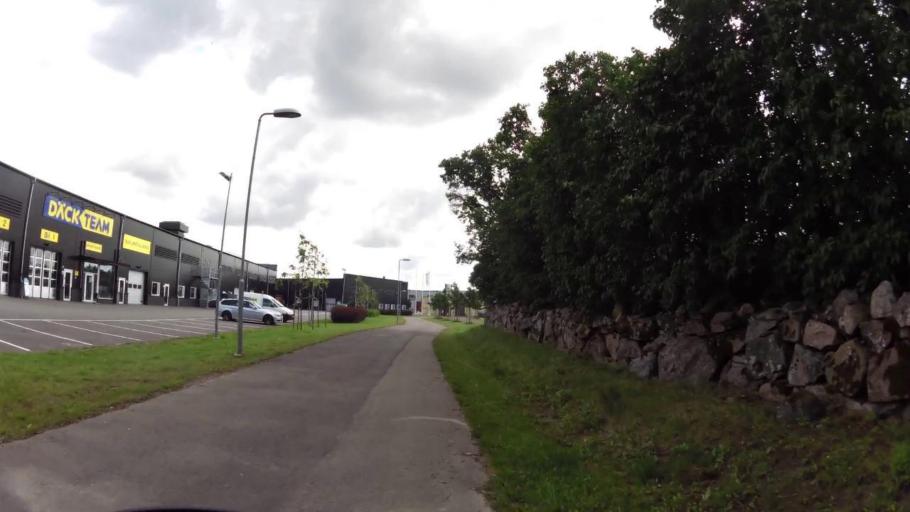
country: SE
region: OEstergoetland
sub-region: Linkopings Kommun
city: Linkoping
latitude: 58.4309
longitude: 15.6053
